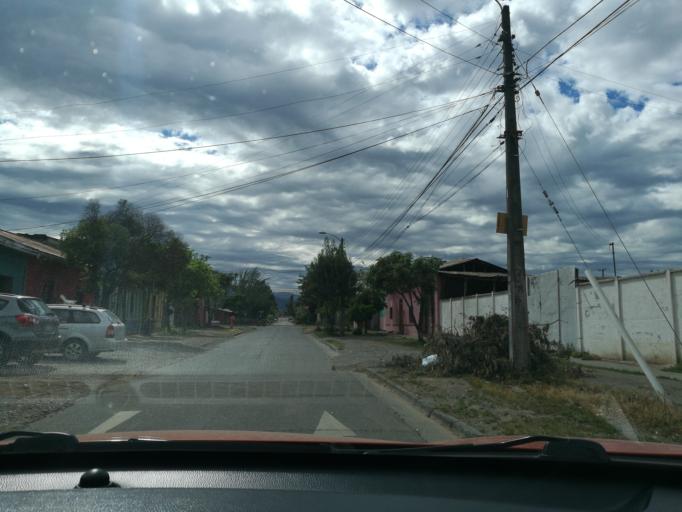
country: CL
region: O'Higgins
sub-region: Provincia de Cachapoal
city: Rancagua
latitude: -34.1634
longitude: -70.7335
